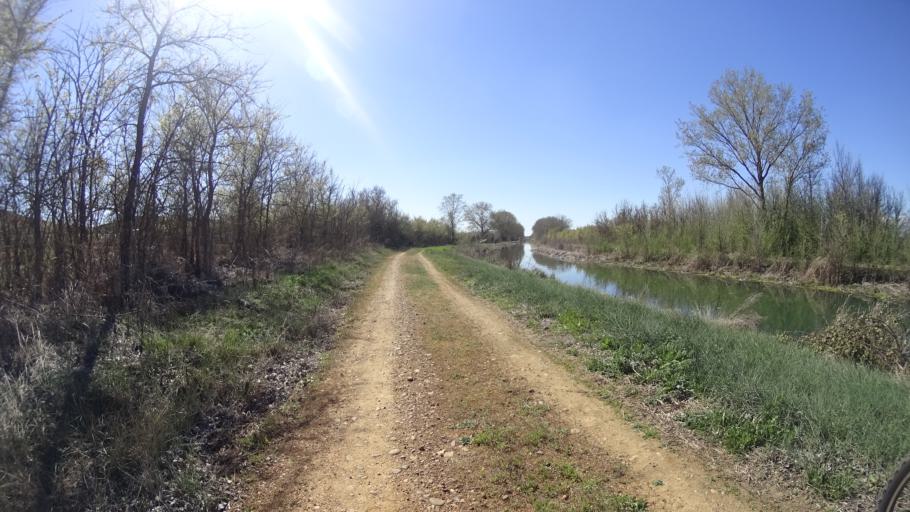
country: ES
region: Castille and Leon
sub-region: Provincia de Palencia
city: Osornillo
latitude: 42.4018
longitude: -4.3279
